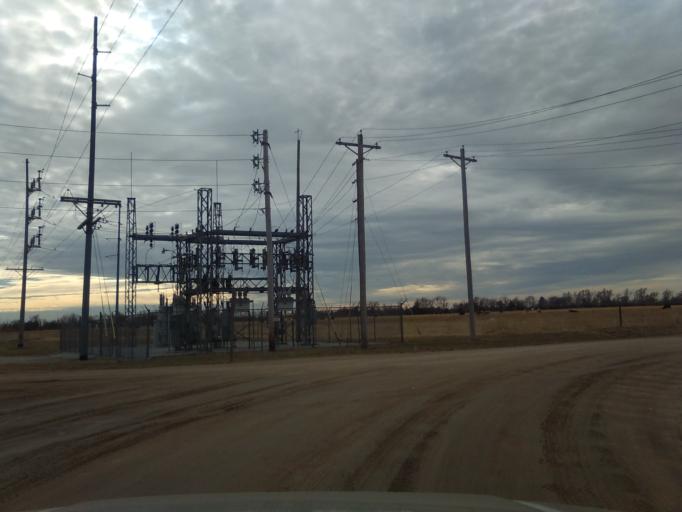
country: US
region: Nebraska
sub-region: Buffalo County
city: Gibbon
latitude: 40.6408
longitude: -98.8759
